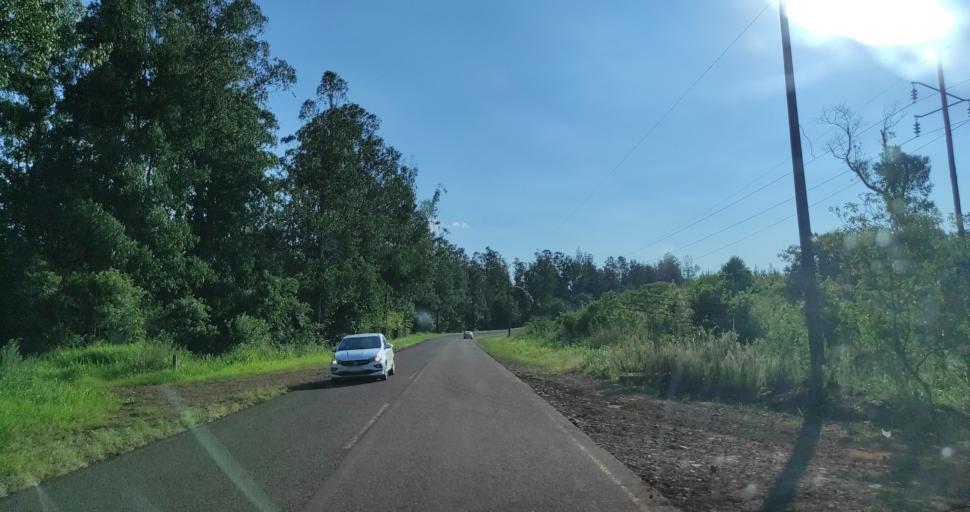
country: AR
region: Misiones
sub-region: Departamento de Eldorado
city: Eldorado
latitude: -26.3983
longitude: -54.3714
